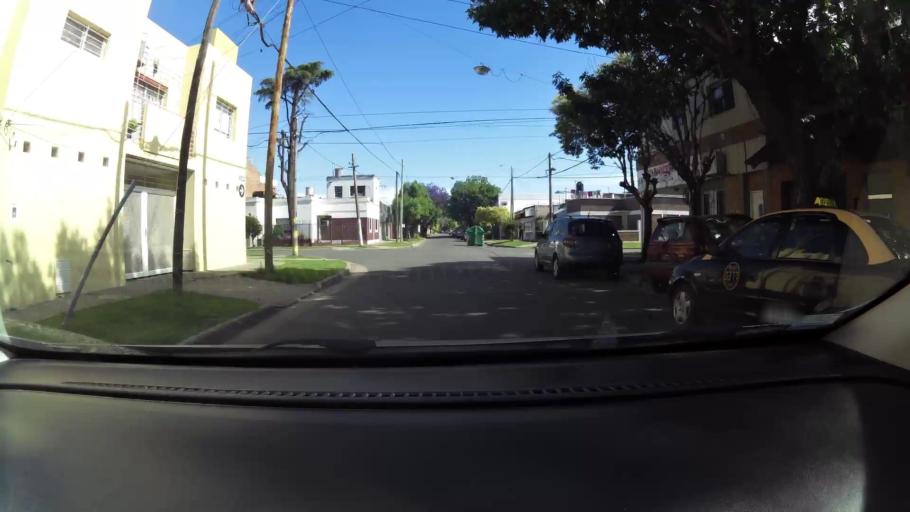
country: AR
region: Santa Fe
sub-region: Departamento de Rosario
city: Rosario
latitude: -32.9390
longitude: -60.7162
